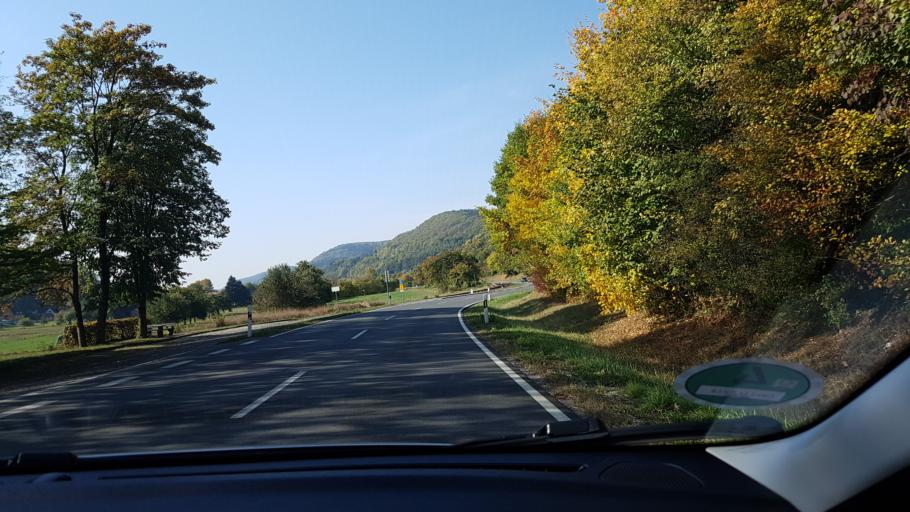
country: DE
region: Bavaria
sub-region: Upper Franconia
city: Unterleinleiter
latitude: 49.8123
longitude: 11.2280
